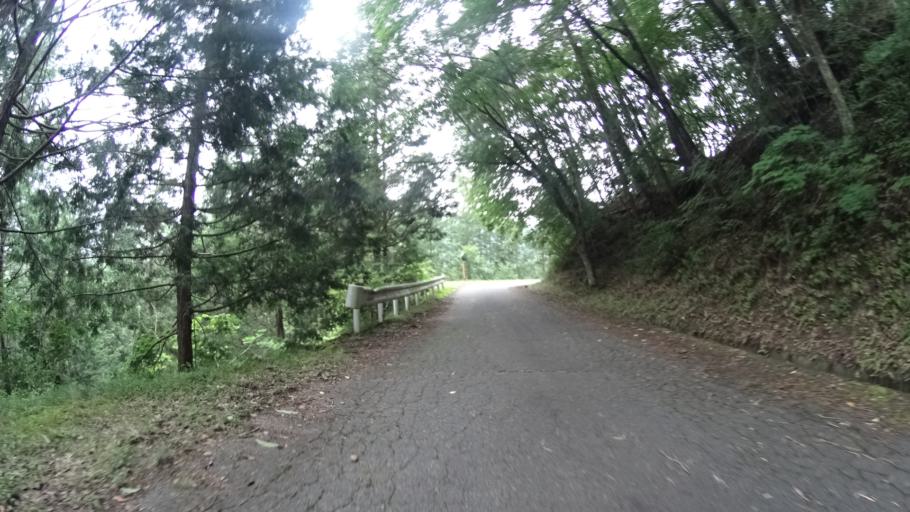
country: JP
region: Yamanashi
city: Kofu-shi
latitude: 35.8107
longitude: 138.5924
